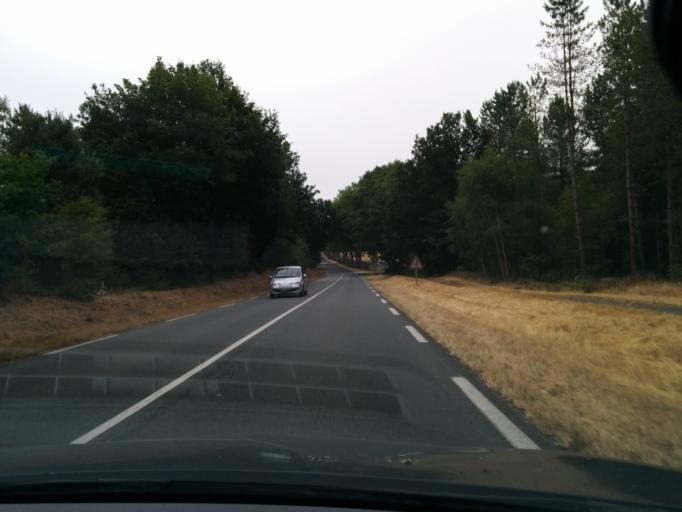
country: FR
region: Ile-de-France
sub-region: Departement des Yvelines
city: Rambouillet
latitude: 48.6709
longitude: 1.7959
